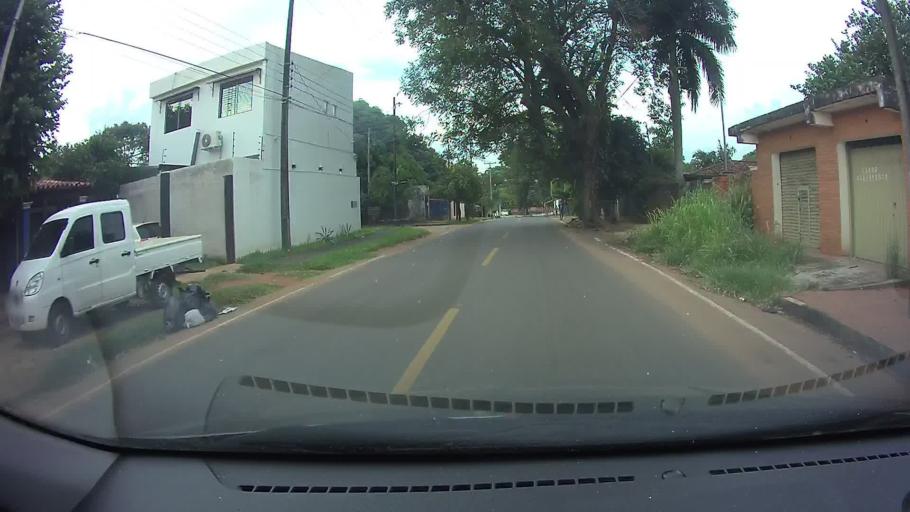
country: PY
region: Central
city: San Lorenzo
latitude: -25.2778
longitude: -57.4787
